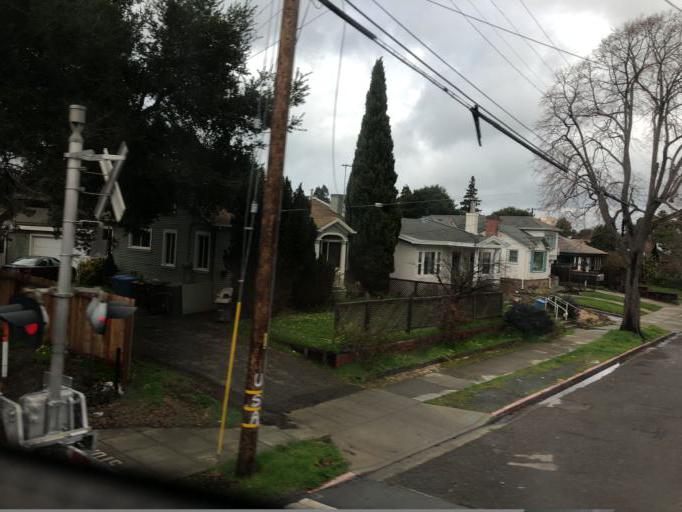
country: US
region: California
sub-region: San Mateo County
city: San Mateo
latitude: 37.5747
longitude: -122.3319
